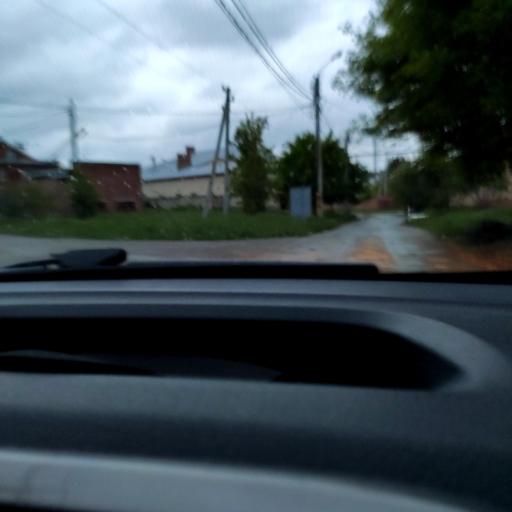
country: RU
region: Samara
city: Tol'yatti
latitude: 53.5422
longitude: 49.3743
